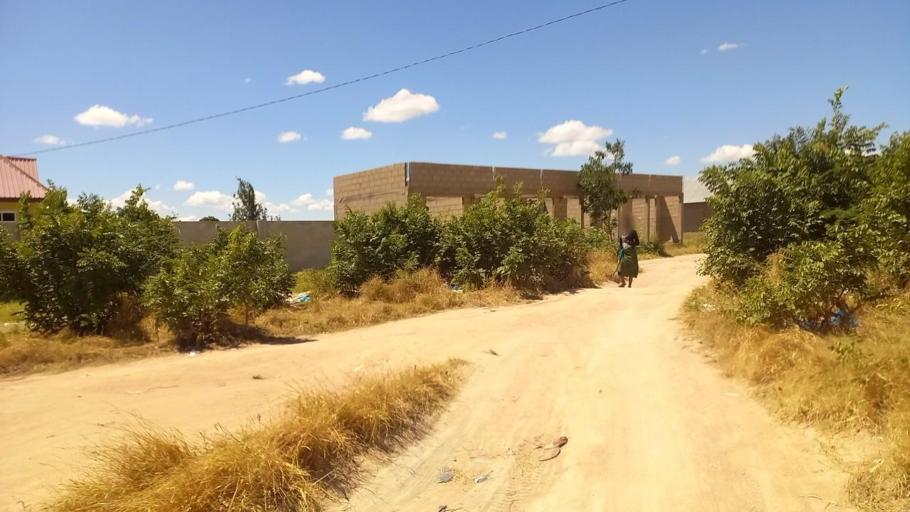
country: TZ
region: Dodoma
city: Dodoma
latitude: -6.1290
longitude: 35.7355
